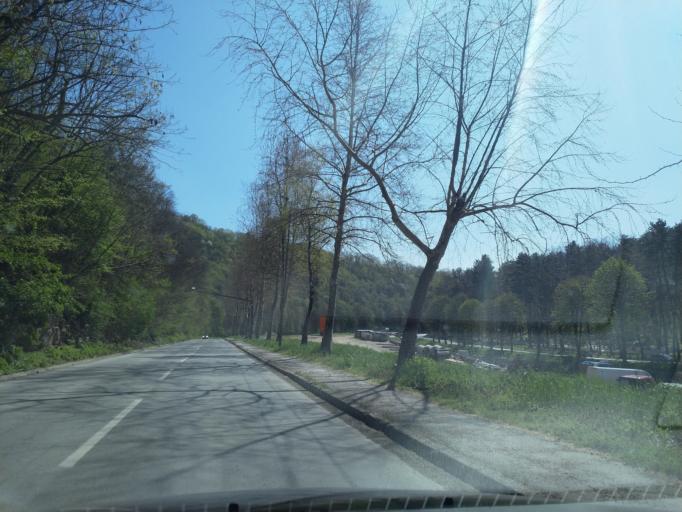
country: RS
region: Central Serbia
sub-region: Kolubarski Okrug
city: Valjevo
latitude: 44.2655
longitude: 19.8784
